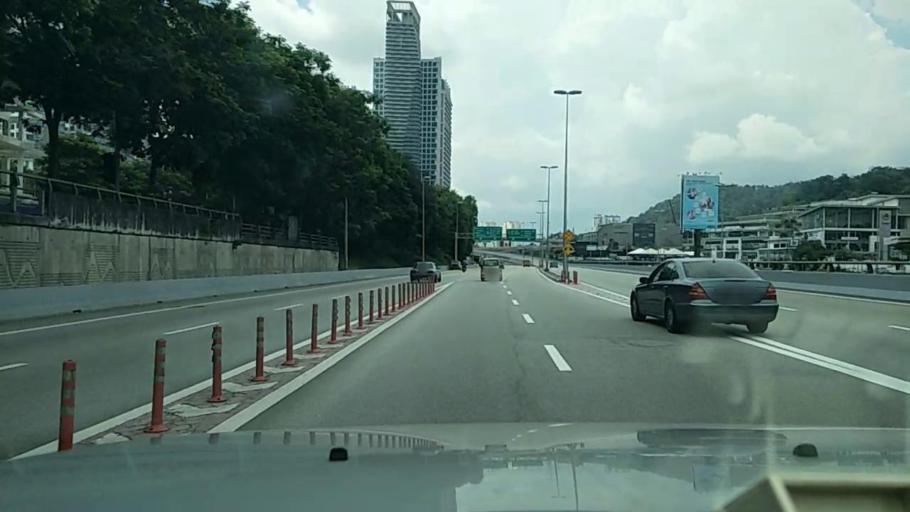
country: MY
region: Selangor
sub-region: Petaling
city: Petaling Jaya
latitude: 3.1603
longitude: 101.6156
